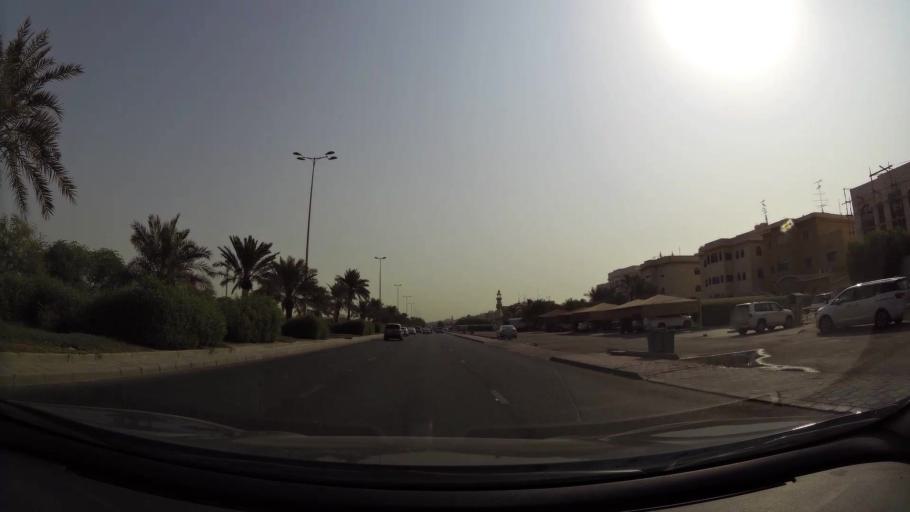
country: KW
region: Al Asimah
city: Ar Rabiyah
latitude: 29.2745
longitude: 47.8724
